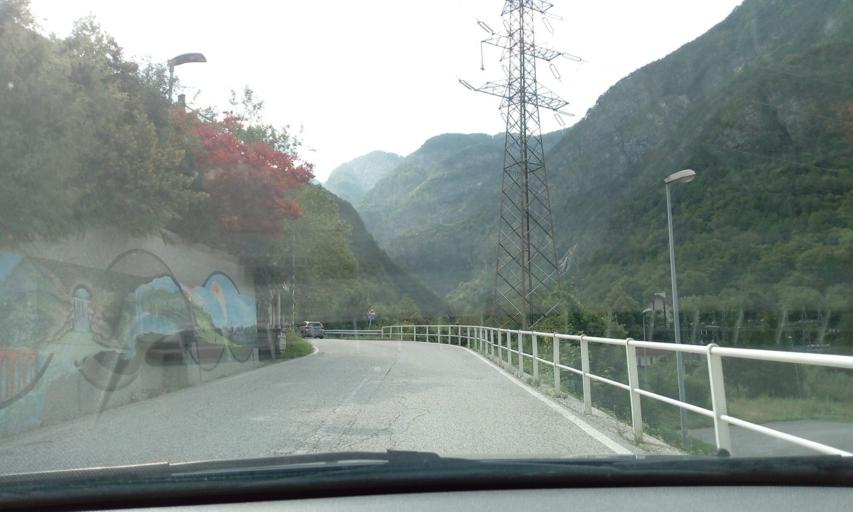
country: IT
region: Friuli Venezia Giulia
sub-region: Provincia di Udine
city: Chiusaforte
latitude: 46.4061
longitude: 13.3161
